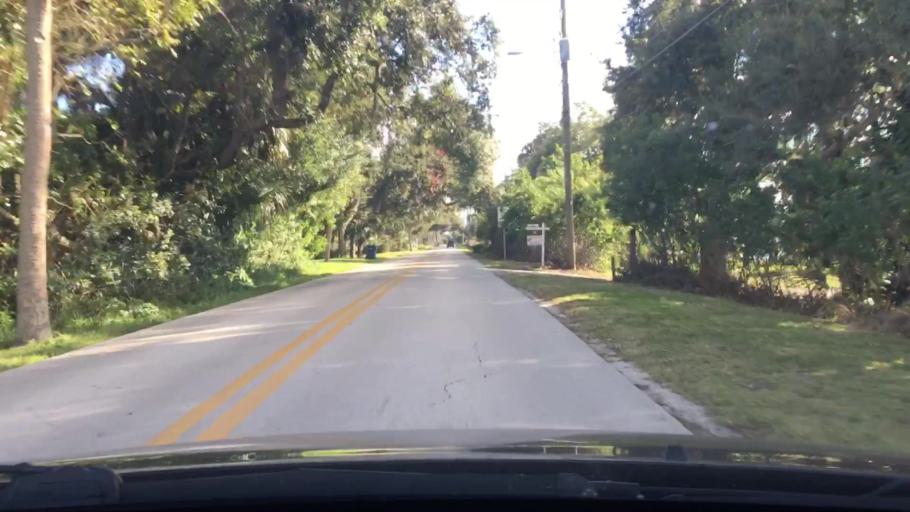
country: US
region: Florida
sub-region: Volusia County
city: Ormond-by-the-Sea
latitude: 29.3522
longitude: -81.0751
